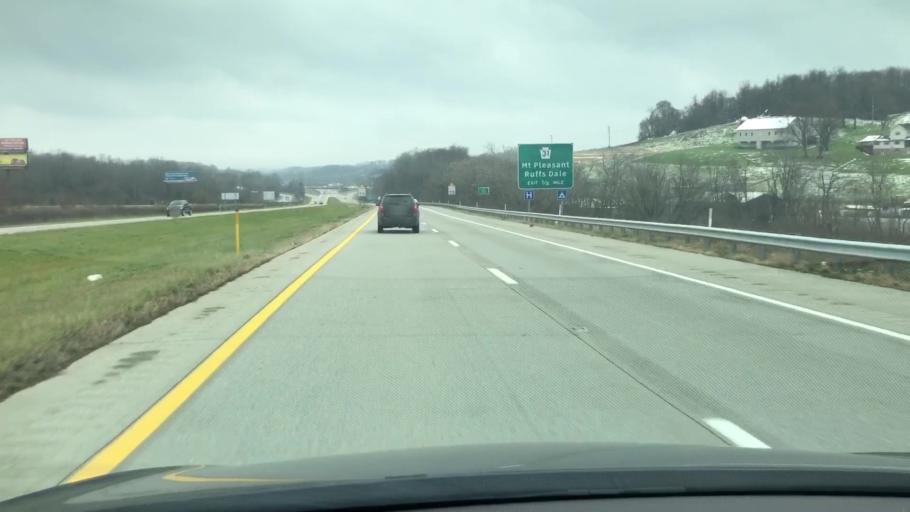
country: US
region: Pennsylvania
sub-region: Westmoreland County
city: Mount Pleasant
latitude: 40.1651
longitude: -79.5608
